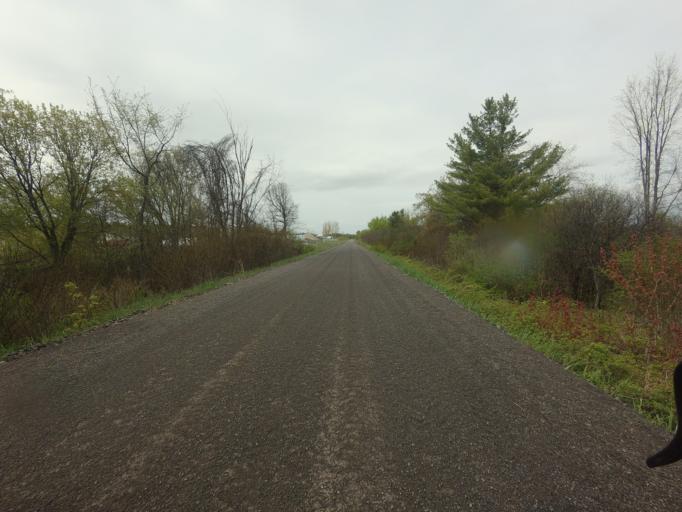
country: CA
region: Ontario
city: Carleton Place
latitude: 45.1530
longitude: -76.1439
